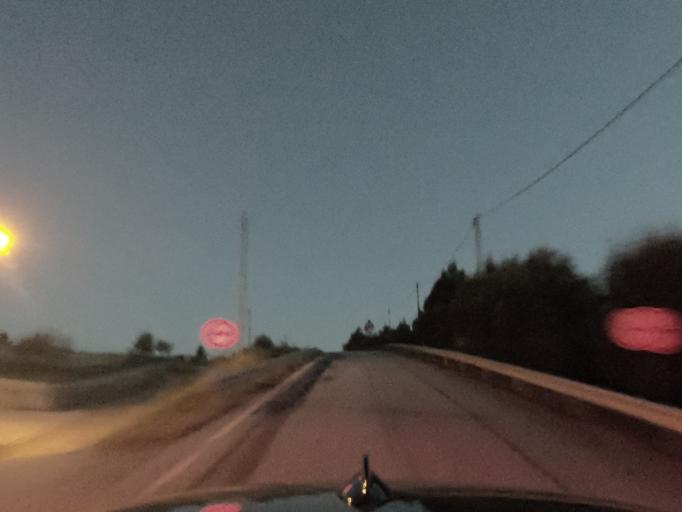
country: PT
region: Vila Real
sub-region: Vila Real
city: Vila Real
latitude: 41.3280
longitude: -7.7011
